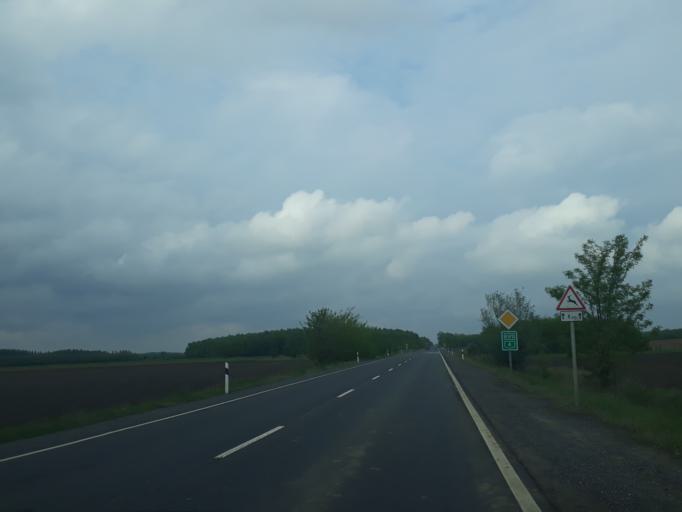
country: HU
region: Szabolcs-Szatmar-Bereg
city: Patroha
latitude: 48.1643
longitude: 22.0313
